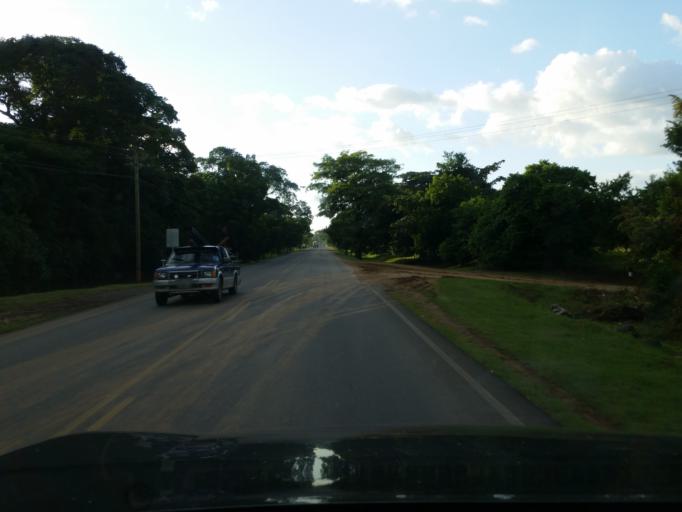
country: NI
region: Granada
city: Nandaime
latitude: 11.7485
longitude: -86.0299
